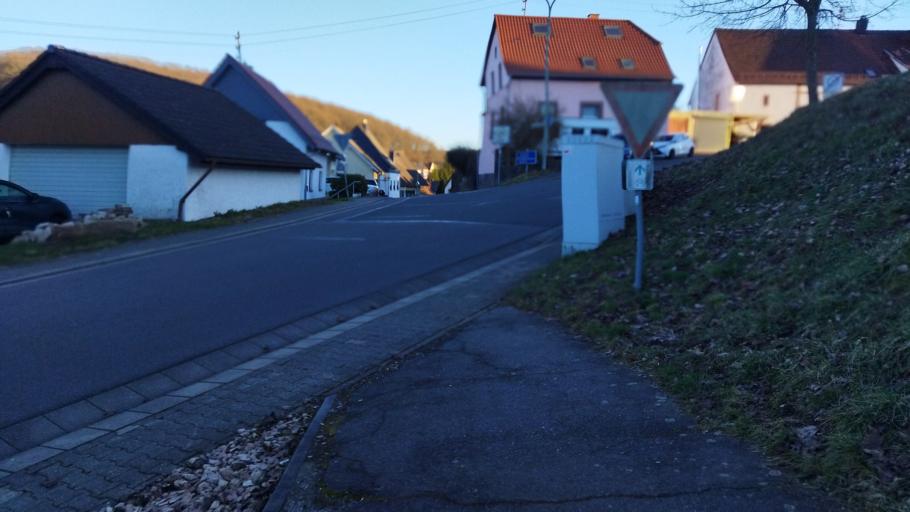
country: DE
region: Rheinland-Pfalz
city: Dittweiler
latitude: 49.4278
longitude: 7.3372
